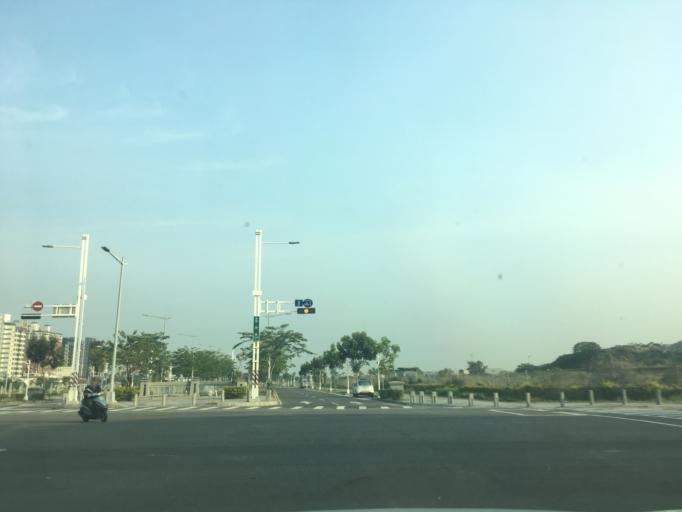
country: TW
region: Taiwan
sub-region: Taichung City
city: Taichung
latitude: 24.1886
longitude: 120.6716
